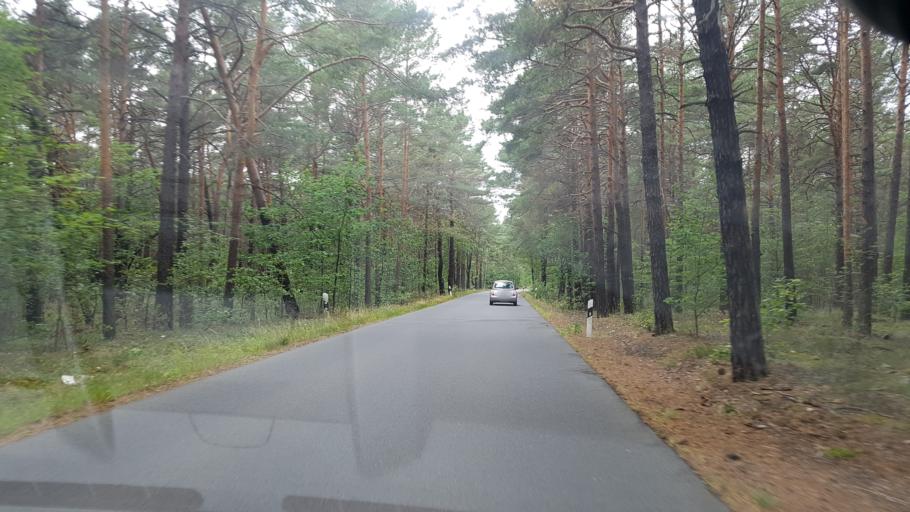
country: DE
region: Brandenburg
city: Spremberg
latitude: 51.5012
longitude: 14.4219
